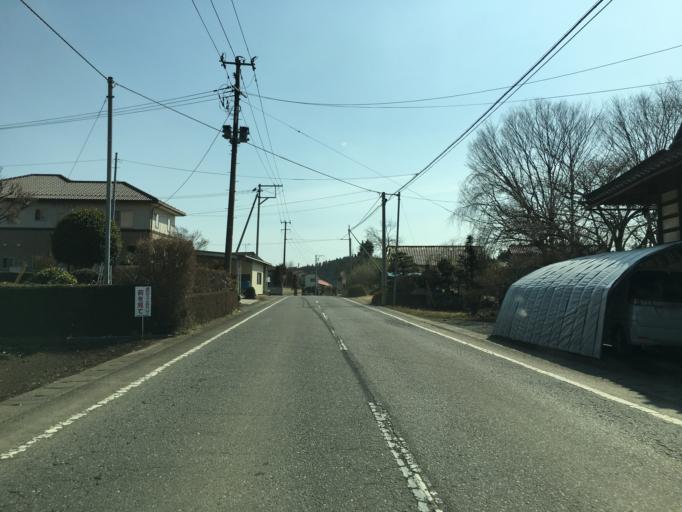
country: JP
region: Fukushima
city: Ishikawa
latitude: 37.1476
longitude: 140.3963
